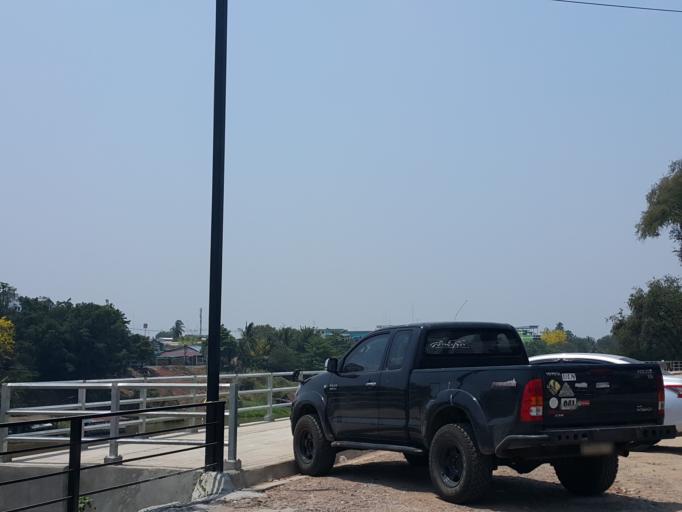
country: TH
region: Phitsanulok
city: Phitsanulok
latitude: 16.8106
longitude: 100.2557
